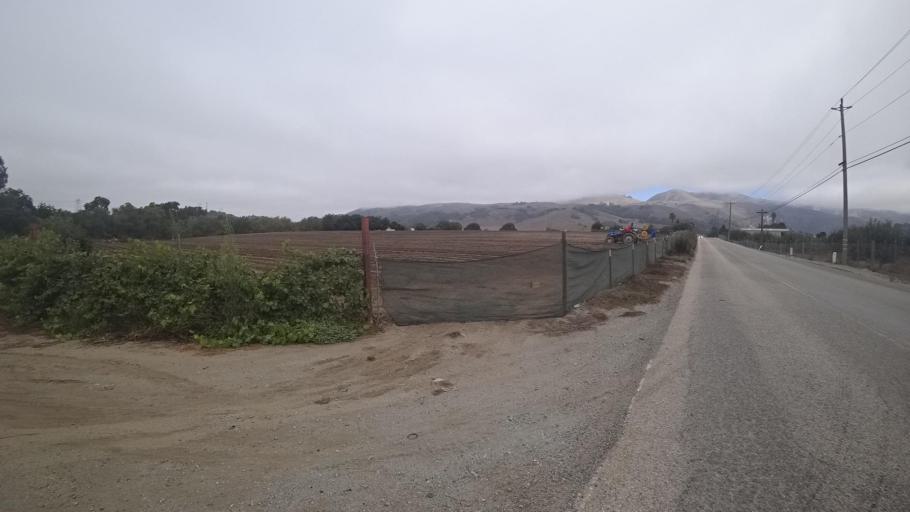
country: US
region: California
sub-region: San Benito County
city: Aromas
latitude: 36.8960
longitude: -121.6457
